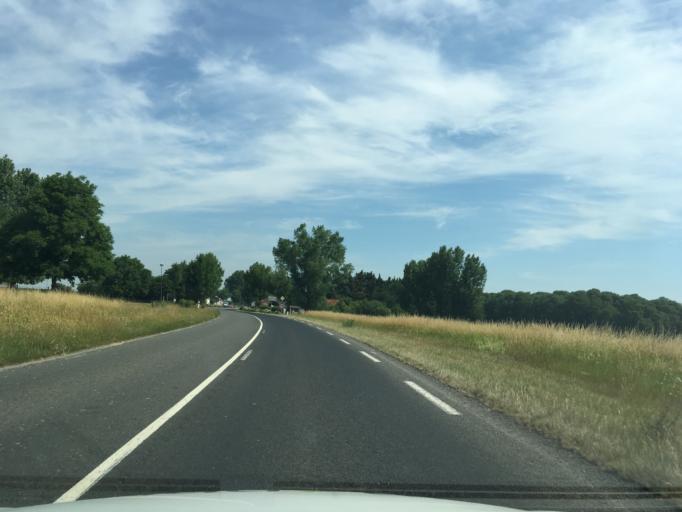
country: FR
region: Picardie
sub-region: Departement de la Somme
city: Chaulnes
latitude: 49.8475
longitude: 2.8751
